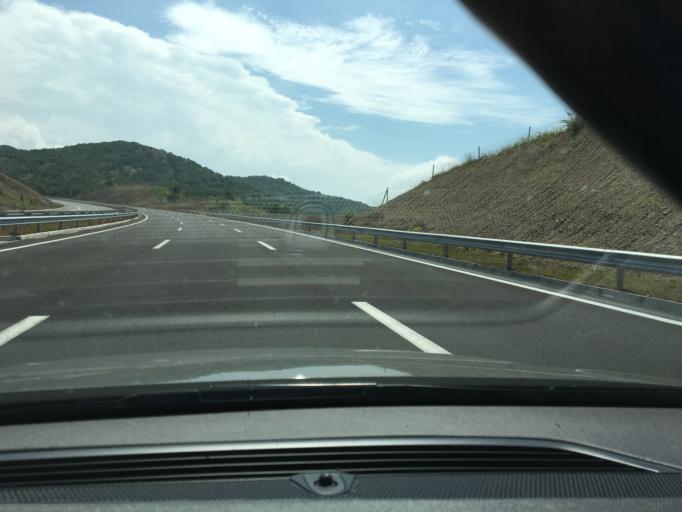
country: MK
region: Petrovec
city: Sredno Konjare
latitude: 41.9444
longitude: 21.7851
